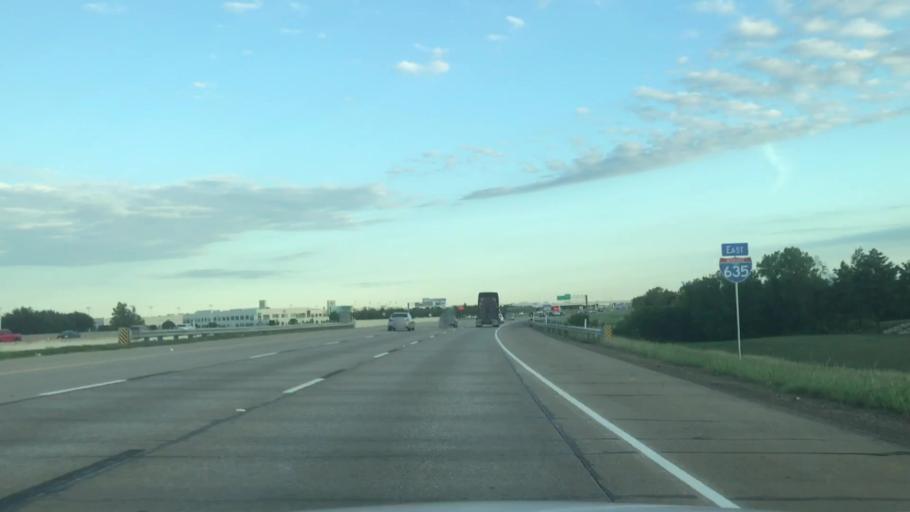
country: US
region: Texas
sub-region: Dallas County
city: Coppell
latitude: 32.9419
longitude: -97.0151
